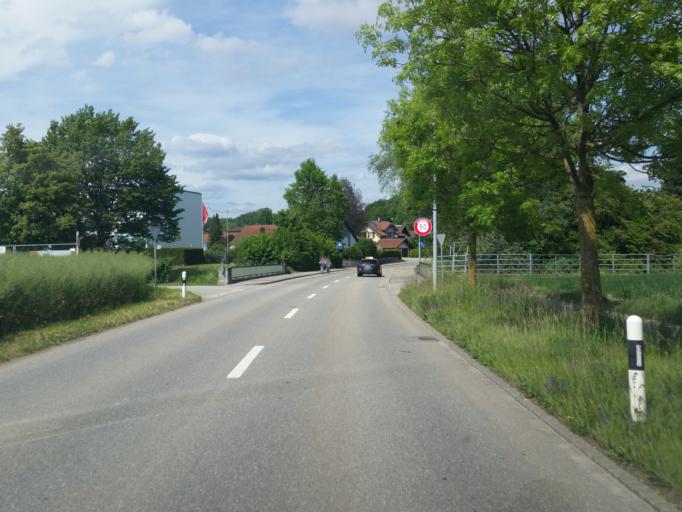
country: CH
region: Aargau
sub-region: Bezirk Muri
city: Waltenschwil
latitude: 47.3348
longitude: 8.2977
